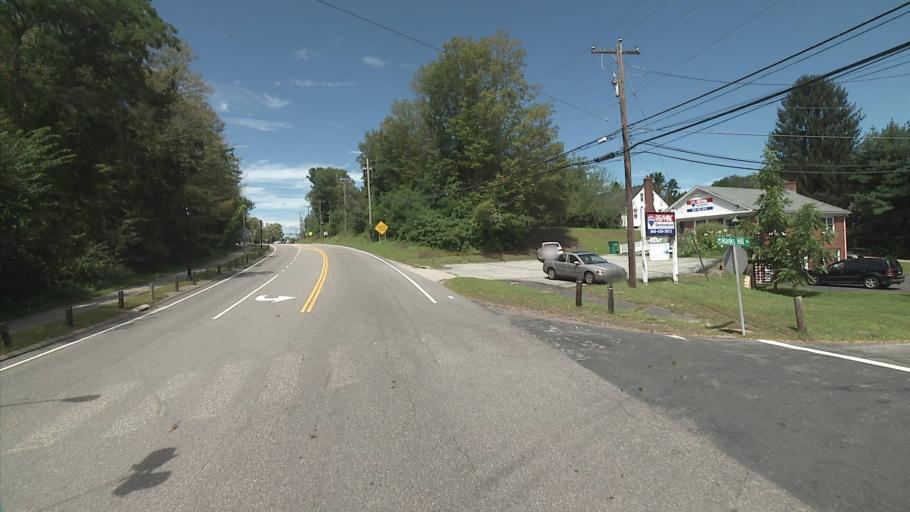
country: US
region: Connecticut
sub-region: Tolland County
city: Storrs
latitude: 41.7996
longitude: -72.2390
